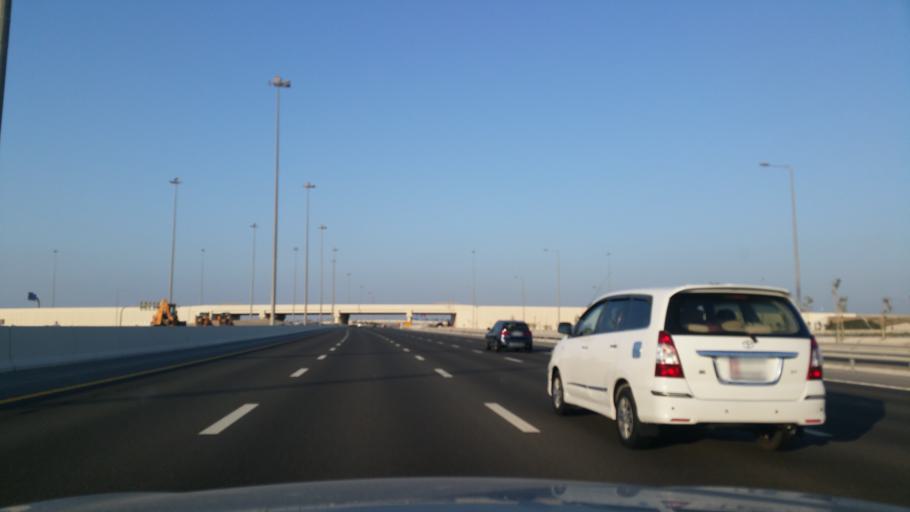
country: QA
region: Al Khawr
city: Al Khawr
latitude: 25.6380
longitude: 51.4919
